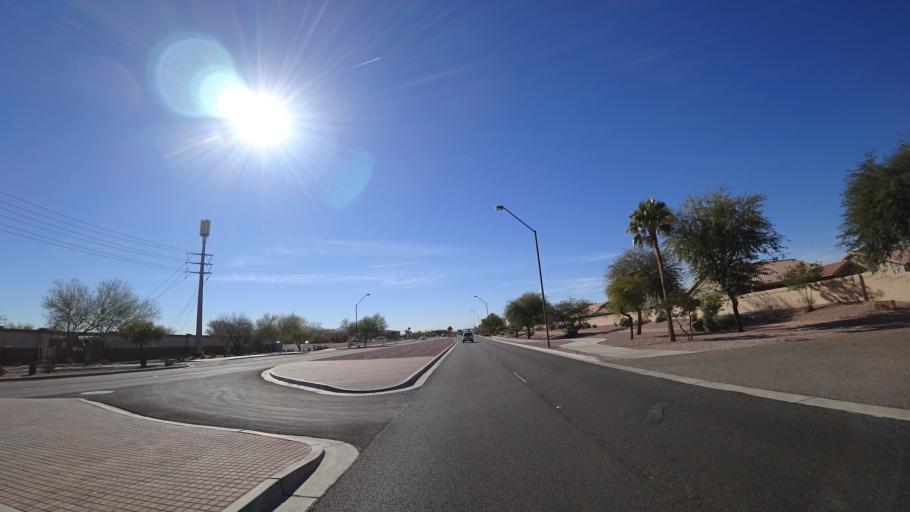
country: US
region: Arizona
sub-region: Maricopa County
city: Litchfield Park
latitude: 33.4793
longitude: -112.3926
